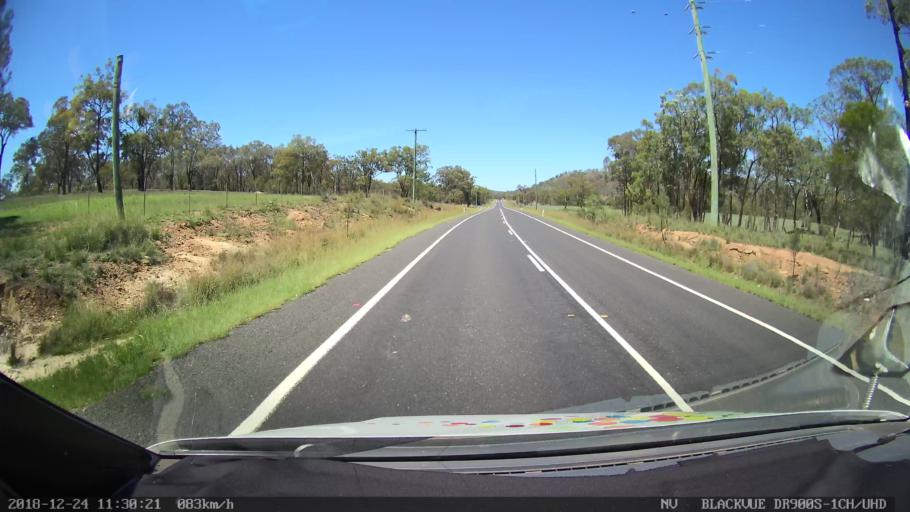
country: AU
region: New South Wales
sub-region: Upper Hunter Shire
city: Merriwa
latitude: -32.2038
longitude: 150.4670
